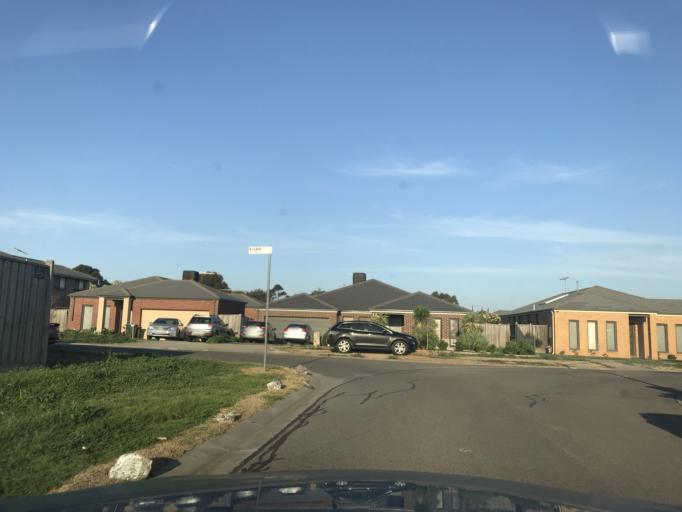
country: AU
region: Victoria
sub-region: Wyndham
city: Williams Landing
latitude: -37.8542
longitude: 144.7272
